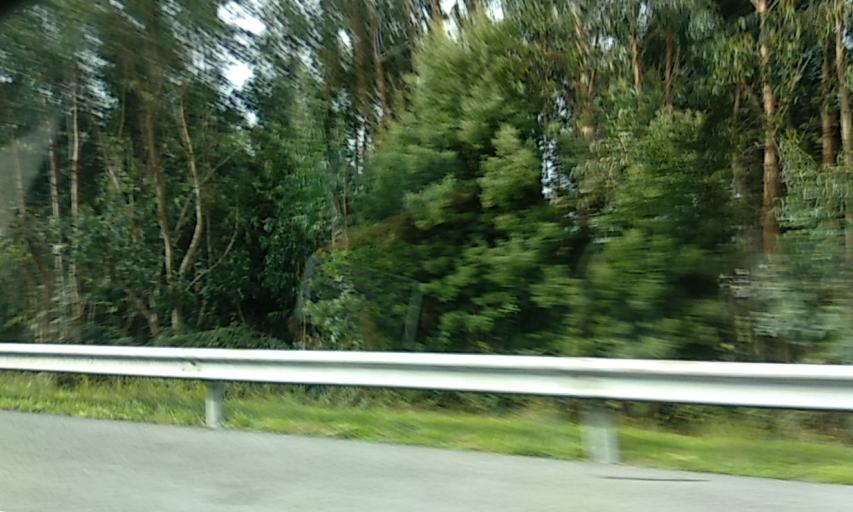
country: PT
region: Braga
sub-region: Vila Nova de Famalicao
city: Vila Nova de Famalicao
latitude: 41.4190
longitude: -8.4936
